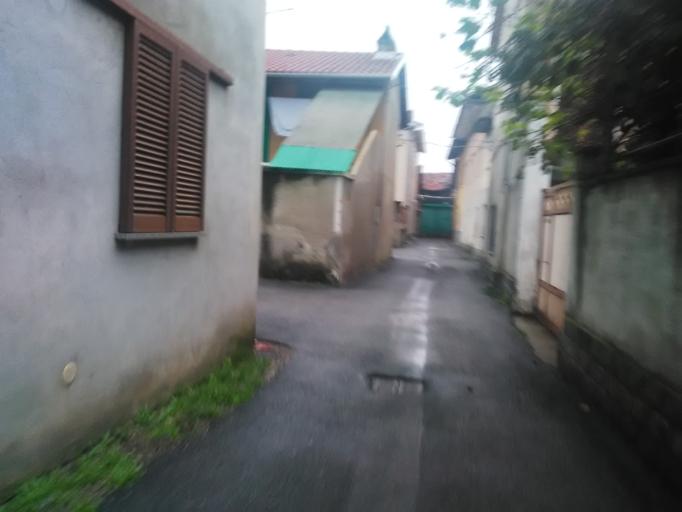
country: IT
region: Piedmont
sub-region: Provincia di Vercelli
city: Cigliano
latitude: 45.3099
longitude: 8.0201
